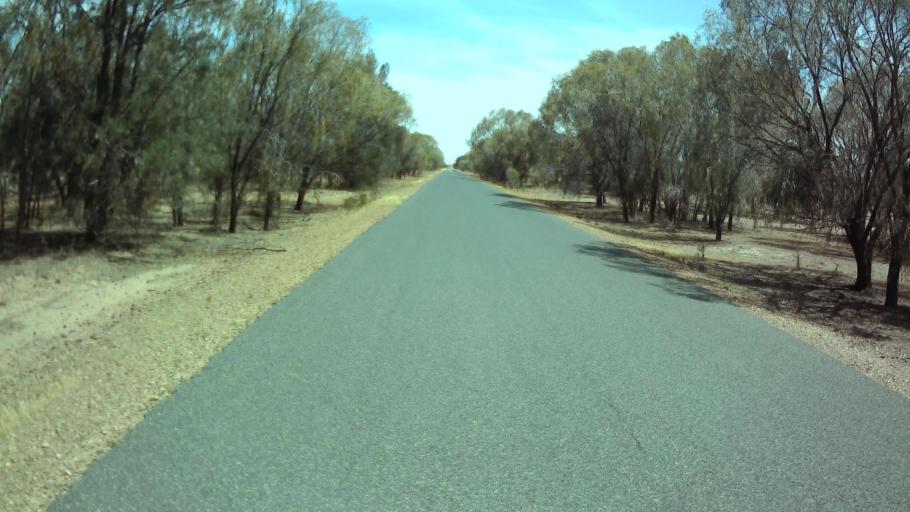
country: AU
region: New South Wales
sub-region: Weddin
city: Grenfell
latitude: -33.8739
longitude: 147.7442
